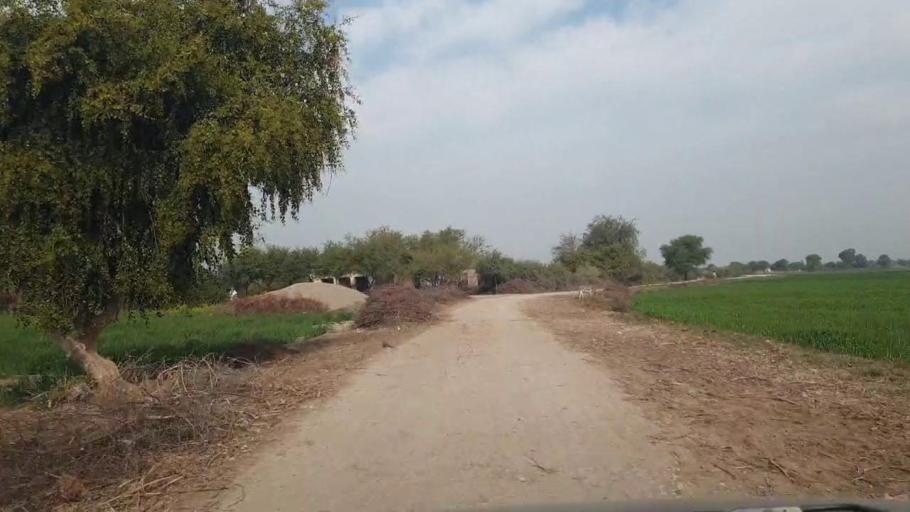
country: PK
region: Sindh
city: Shahdadpur
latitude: 25.9332
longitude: 68.6812
